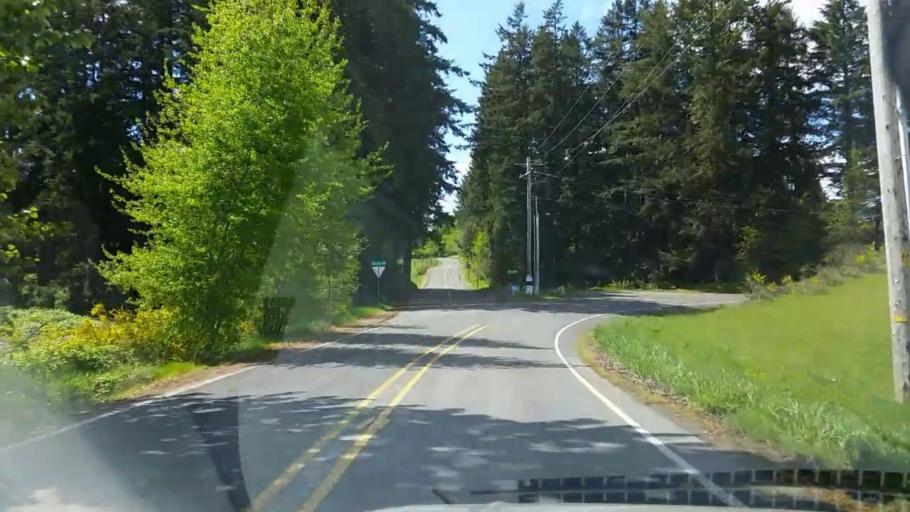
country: US
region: Washington
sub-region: Pierce County
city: Key Center
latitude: 47.3408
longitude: -122.7469
